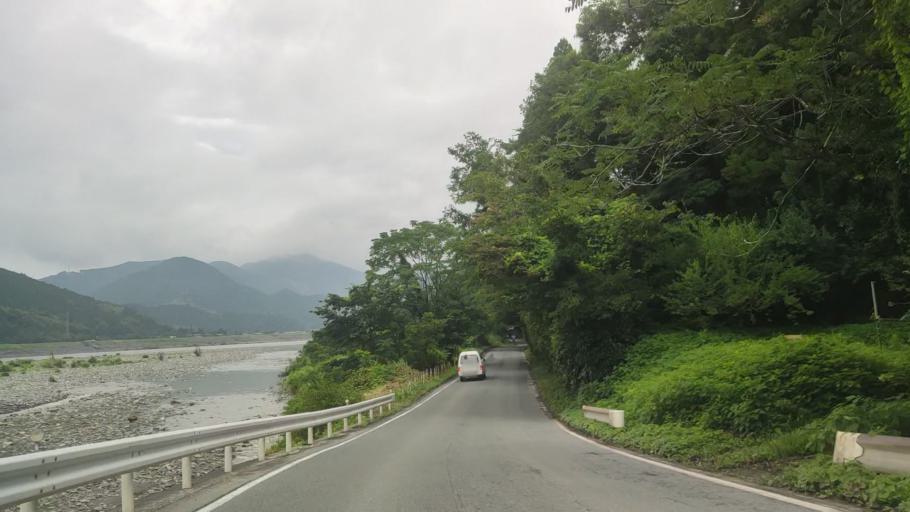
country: JP
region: Shizuoka
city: Fujinomiya
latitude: 35.2126
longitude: 138.5447
